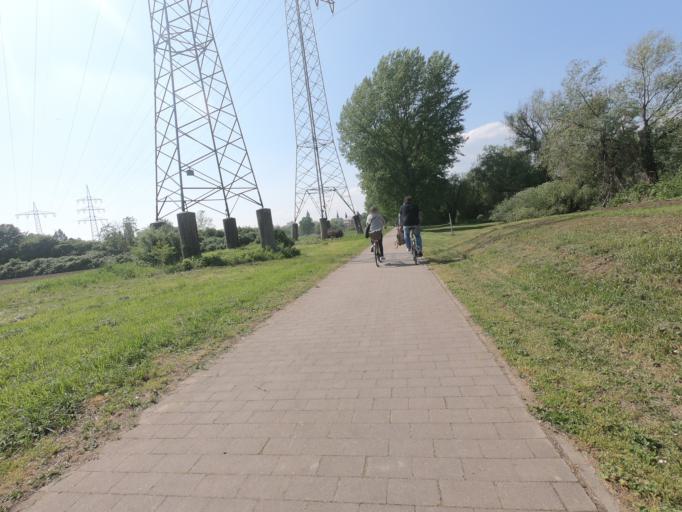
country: DE
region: Hesse
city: Kelsterbach
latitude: 50.0978
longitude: 8.5572
